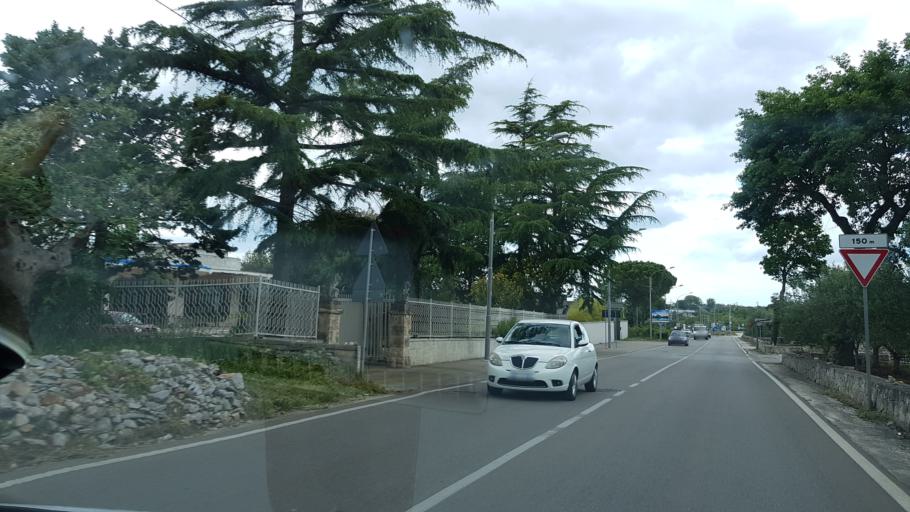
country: IT
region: Apulia
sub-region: Provincia di Bari
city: Locorotondo
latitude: 40.7619
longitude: 17.3303
